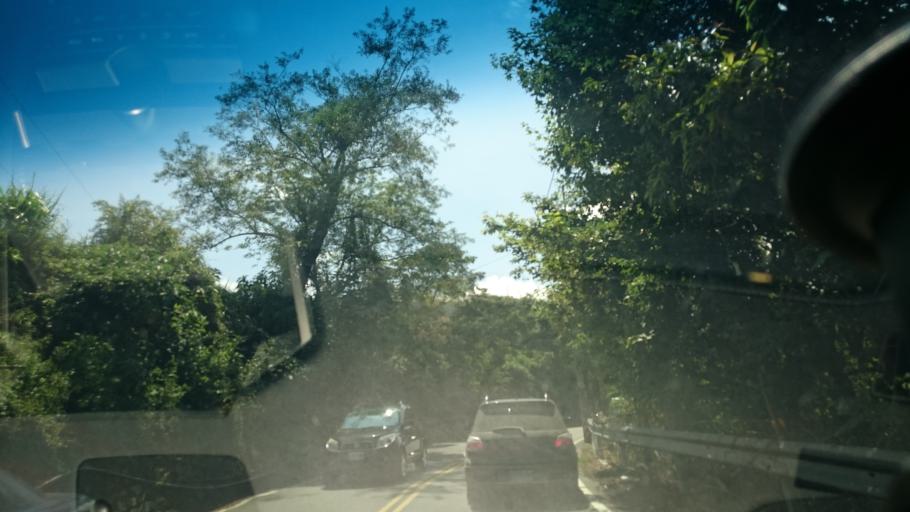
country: TW
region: Taiwan
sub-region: Nantou
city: Puli
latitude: 24.0296
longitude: 121.1453
